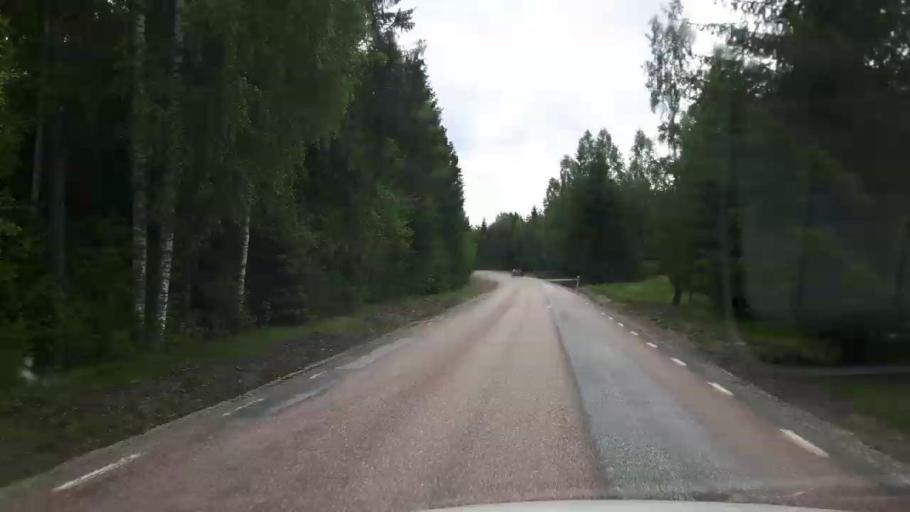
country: SE
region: Vaestmanland
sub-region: Skinnskattebergs Kommun
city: Skinnskatteberg
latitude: 59.8310
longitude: 15.8329
